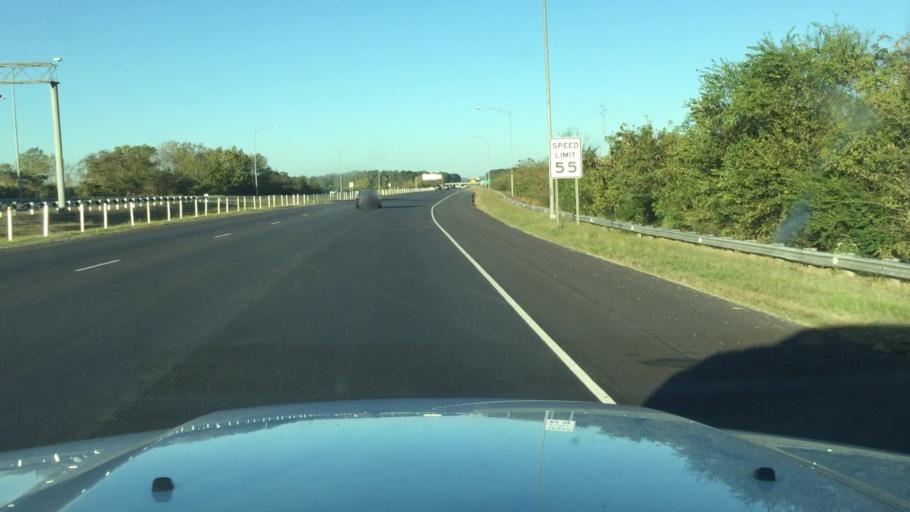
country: US
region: Alabama
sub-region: Etowah County
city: Gadsden
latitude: 33.9918
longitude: -86.0096
